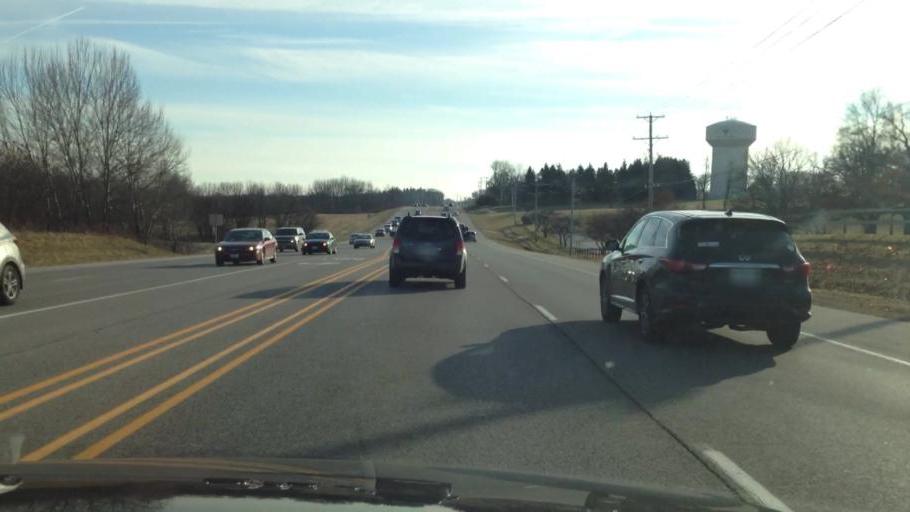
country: US
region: Illinois
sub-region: Kane County
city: Sleepy Hollow
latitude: 42.1155
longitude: -88.3352
